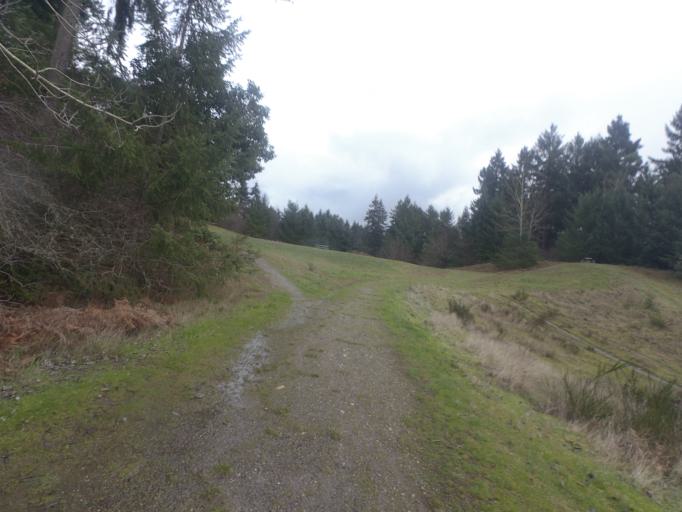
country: US
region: Washington
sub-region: Pierce County
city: University Place
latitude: 47.2243
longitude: -122.5491
